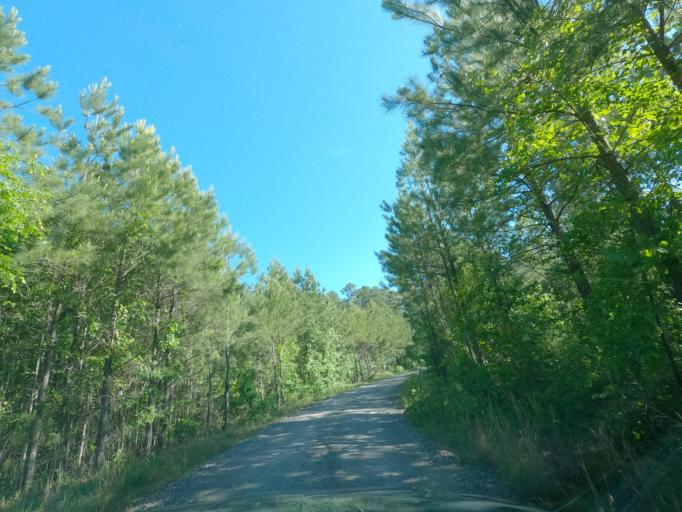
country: US
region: Georgia
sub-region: Columbia County
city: Evans
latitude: 33.6121
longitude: -82.1132
